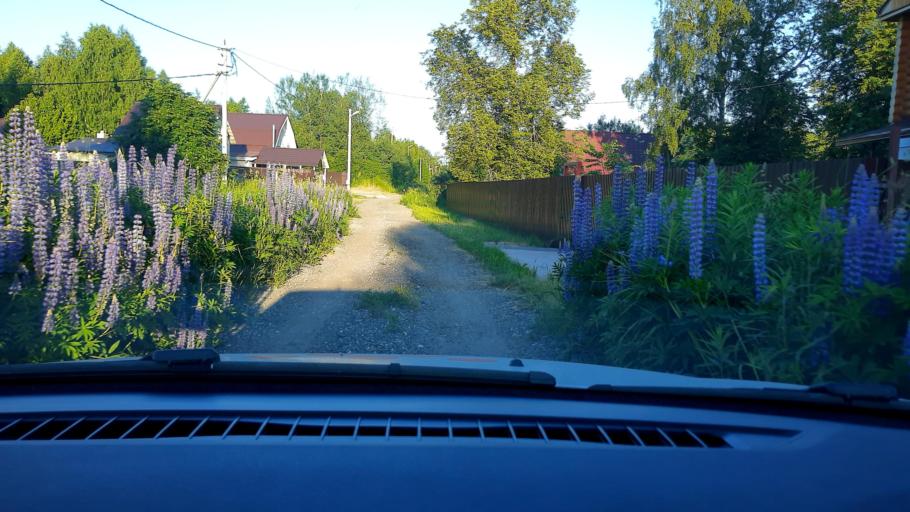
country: RU
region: Nizjnij Novgorod
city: Kstovo
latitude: 56.3086
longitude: 44.2729
